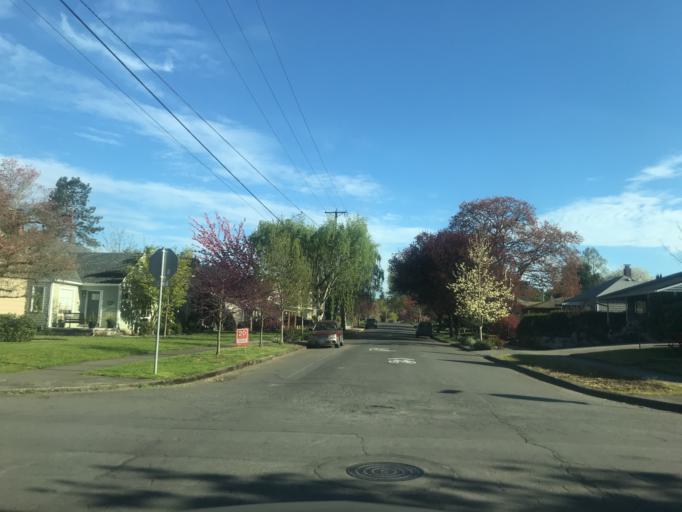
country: US
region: Oregon
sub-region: Multnomah County
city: Lents
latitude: 45.4999
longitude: -122.5857
